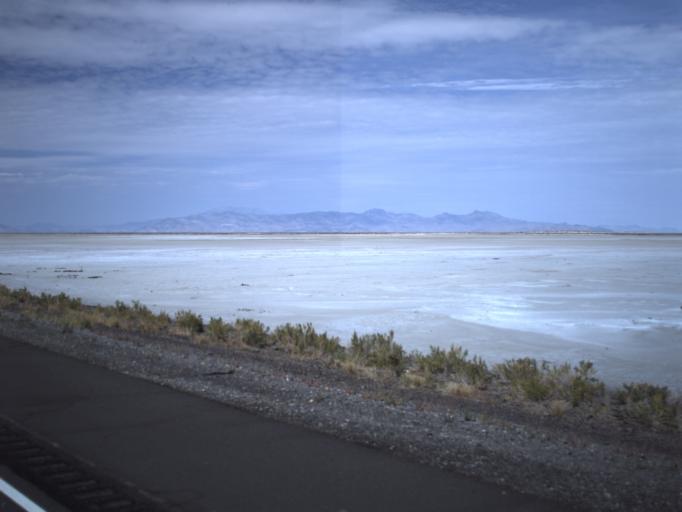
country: US
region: Utah
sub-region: Tooele County
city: Wendover
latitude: 40.7307
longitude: -113.4543
